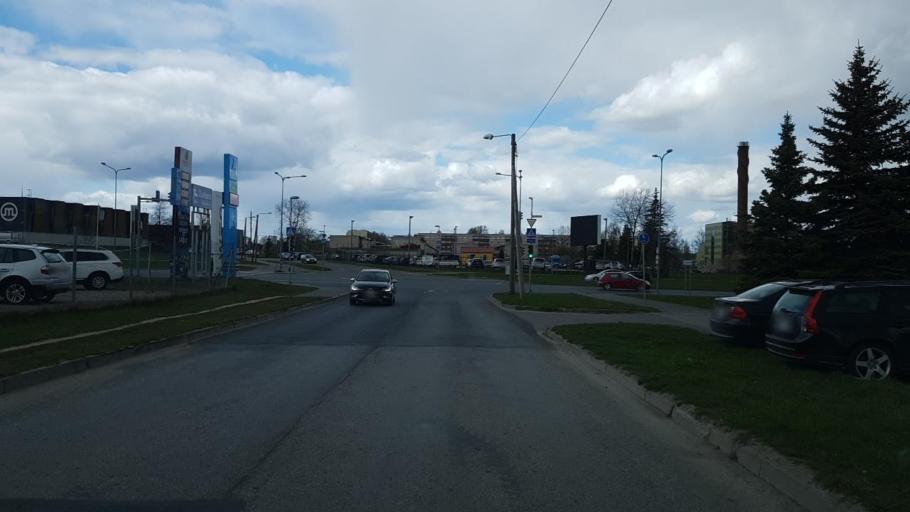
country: EE
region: Tartu
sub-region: UElenurme vald
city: Ulenurme
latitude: 58.3422
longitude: 26.7251
